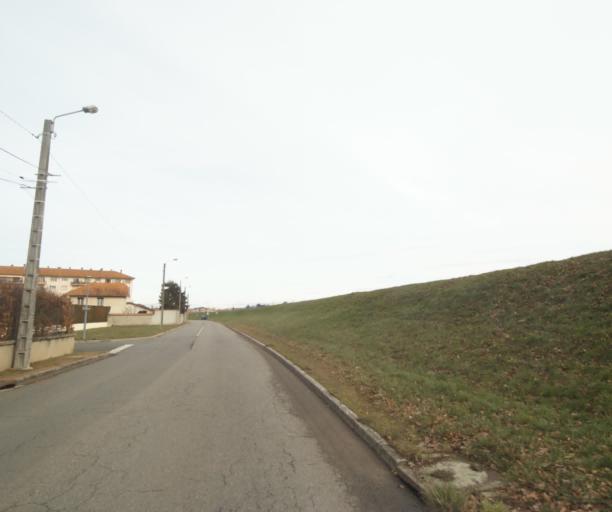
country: FR
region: Rhone-Alpes
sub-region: Departement de la Loire
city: Roanne
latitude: 46.0237
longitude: 4.0711
